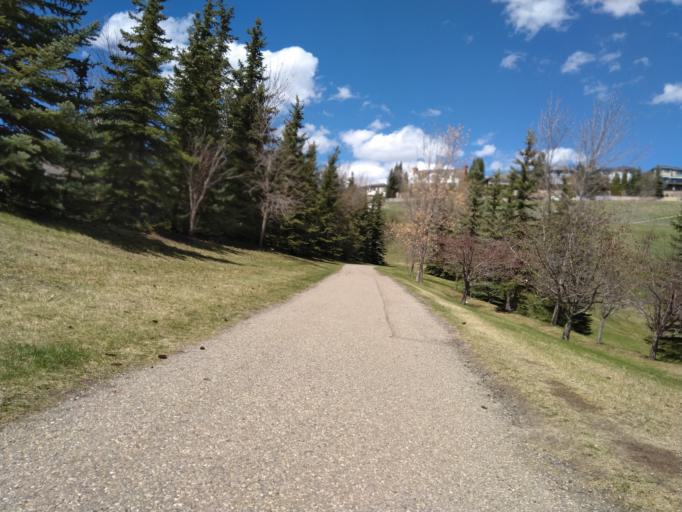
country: CA
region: Alberta
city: Calgary
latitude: 51.0194
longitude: -114.1755
